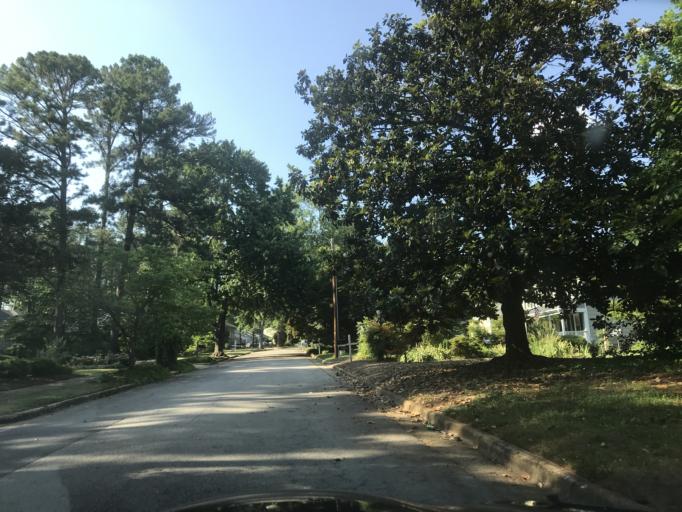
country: US
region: North Carolina
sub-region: Wake County
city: Raleigh
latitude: 35.8588
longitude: -78.6035
